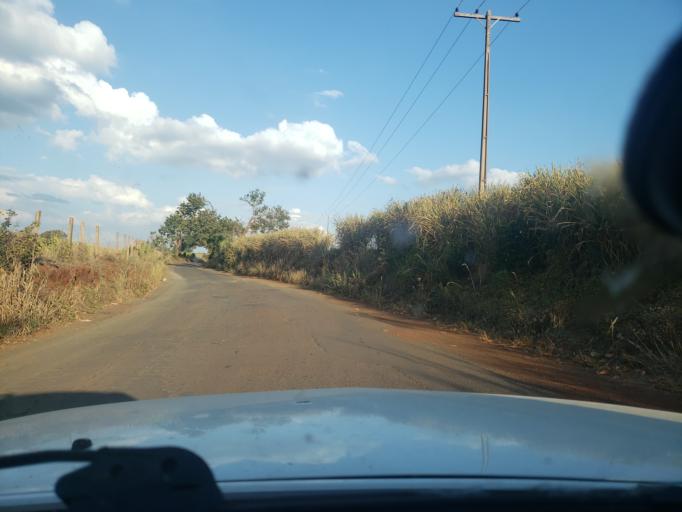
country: BR
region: Sao Paulo
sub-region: Mogi-Mirim
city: Mogi Mirim
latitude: -22.4704
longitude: -46.9292
